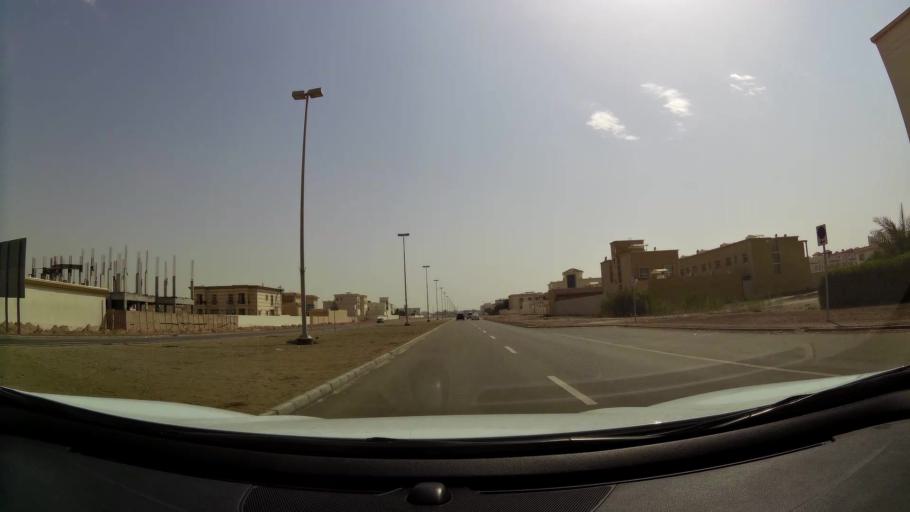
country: AE
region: Abu Dhabi
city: Abu Dhabi
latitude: 24.3235
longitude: 54.5518
